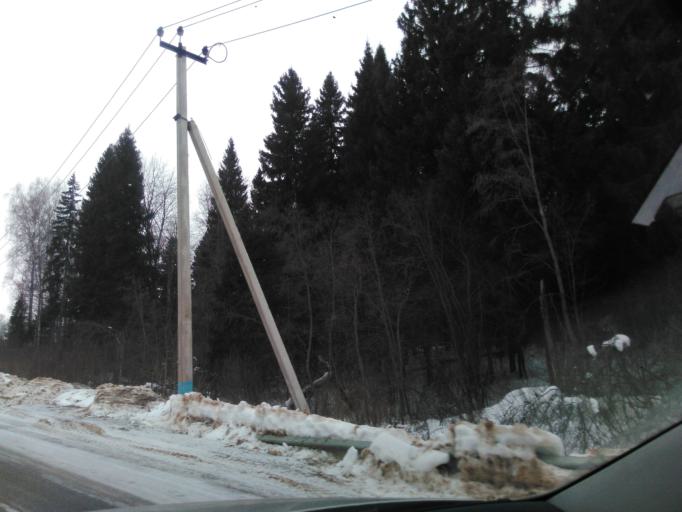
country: RU
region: Moskovskaya
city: Podosinki
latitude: 56.2726
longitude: 37.6172
